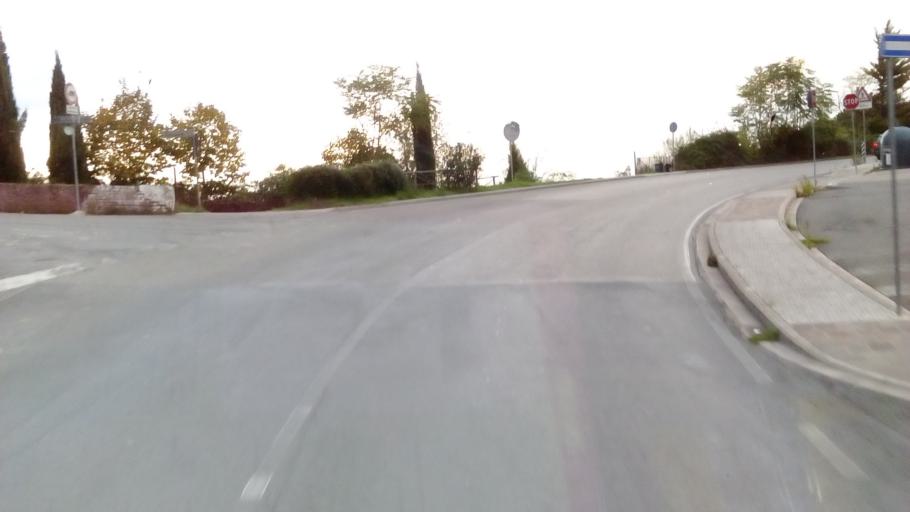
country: IT
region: Tuscany
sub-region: Province of Florence
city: Castelfiorentino
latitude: 43.6075
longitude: 10.9731
